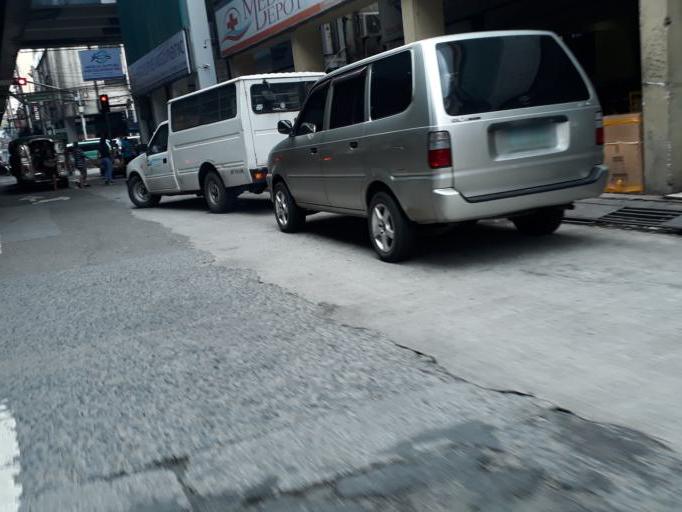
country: PH
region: Metro Manila
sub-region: City of Manila
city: Manila
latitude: 14.6104
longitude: 120.9826
